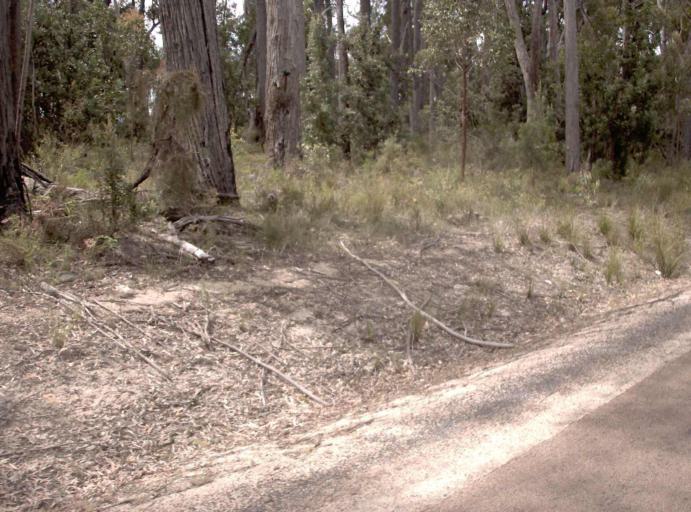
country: AU
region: New South Wales
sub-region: Bega Valley
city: Eden
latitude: -37.5037
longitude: 149.5346
